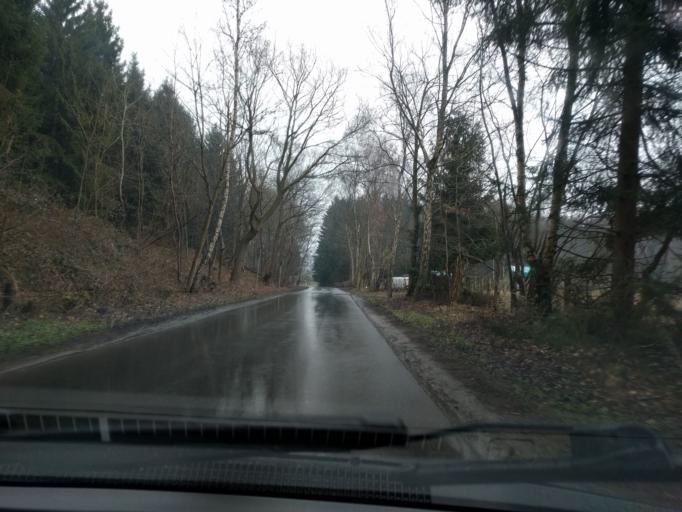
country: DE
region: Lower Saxony
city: Bendestorf
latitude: 53.3636
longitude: 9.9616
